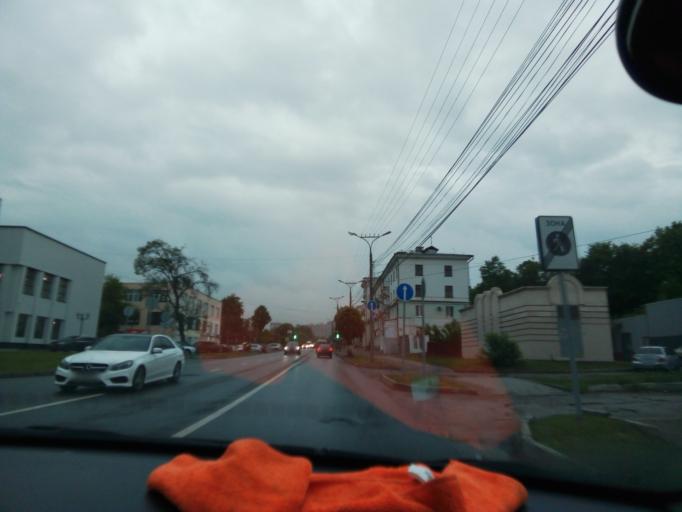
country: RU
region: Chuvashia
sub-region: Cheboksarskiy Rayon
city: Cheboksary
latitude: 56.1425
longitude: 47.2531
